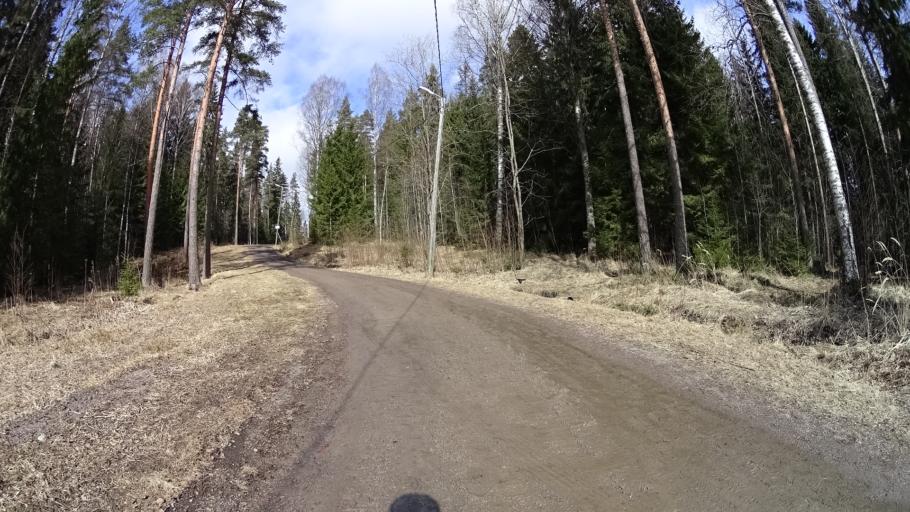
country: FI
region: Uusimaa
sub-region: Helsinki
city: Kilo
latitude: 60.2966
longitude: 24.8179
